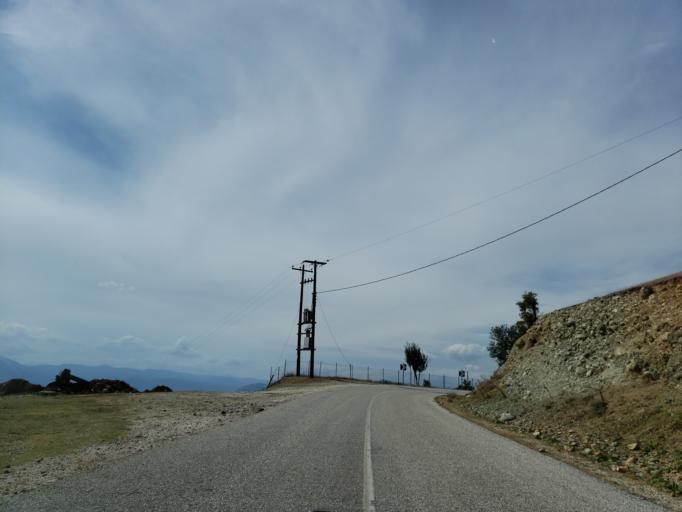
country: GR
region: Thessaly
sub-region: Trikala
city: Kastraki
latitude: 39.7695
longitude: 21.6636
